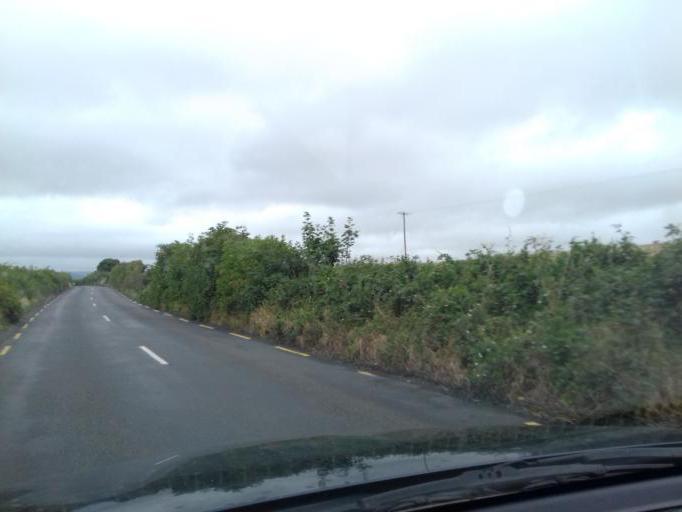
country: IE
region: Leinster
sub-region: County Carlow
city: Bagenalstown
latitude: 52.7168
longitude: -6.9620
